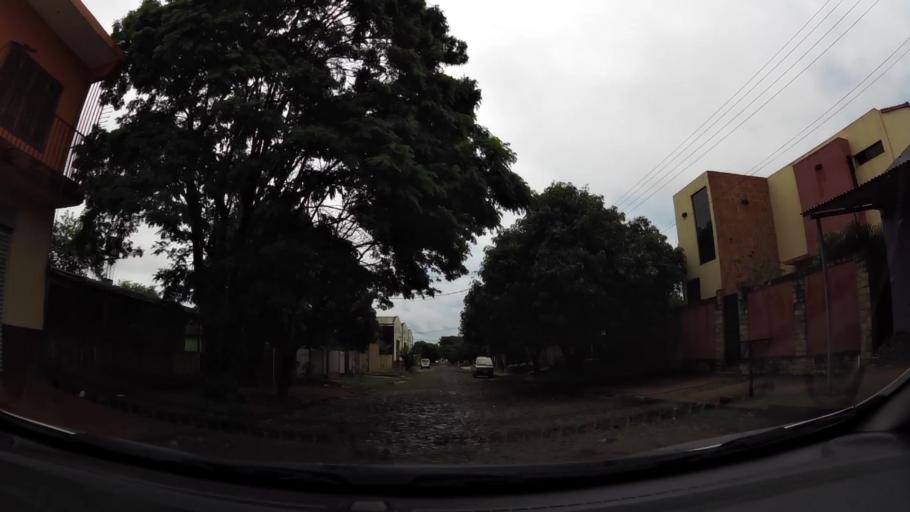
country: PY
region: Alto Parana
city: Presidente Franco
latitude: -25.5153
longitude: -54.6725
